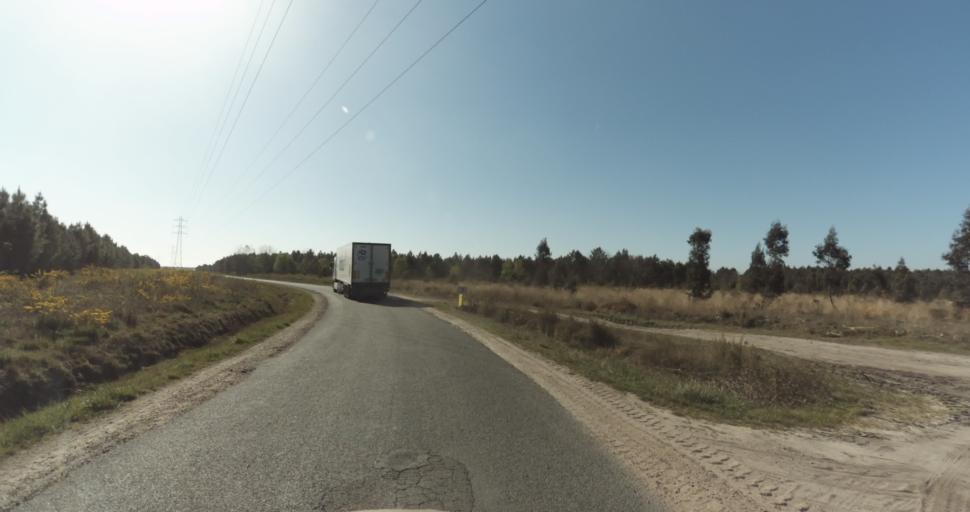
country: FR
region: Aquitaine
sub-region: Departement de la Gironde
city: Marcheprime
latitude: 44.7509
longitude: -0.8479
